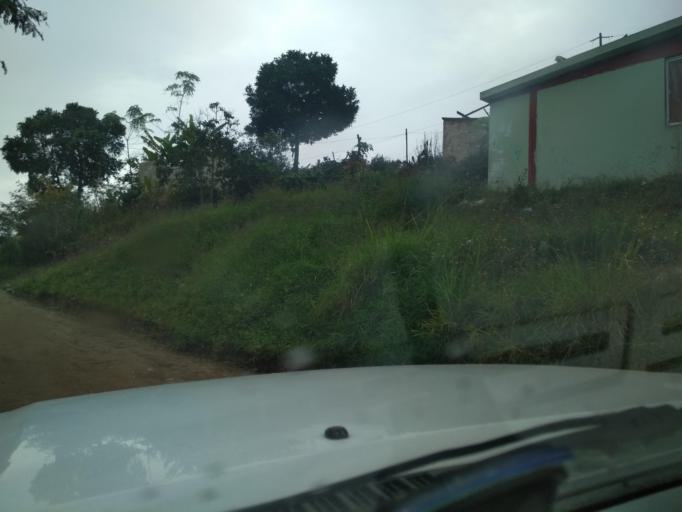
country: MX
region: Veracruz
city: El Castillo
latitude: 19.5397
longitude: -96.8327
